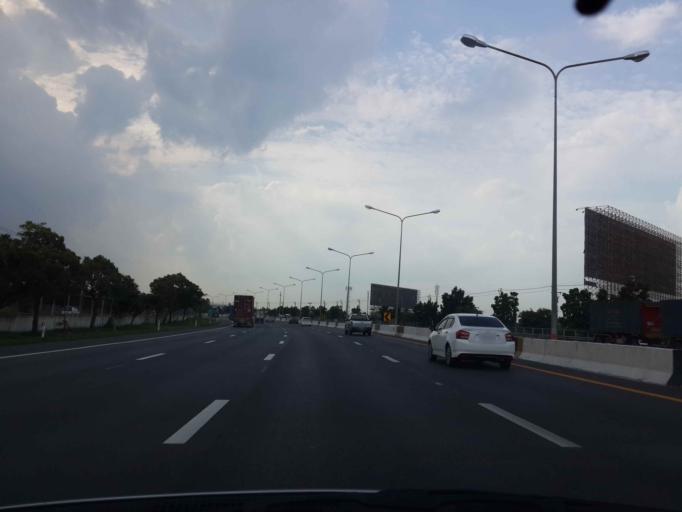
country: TH
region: Bangkok
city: Lat Krabang
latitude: 13.7309
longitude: 100.8095
